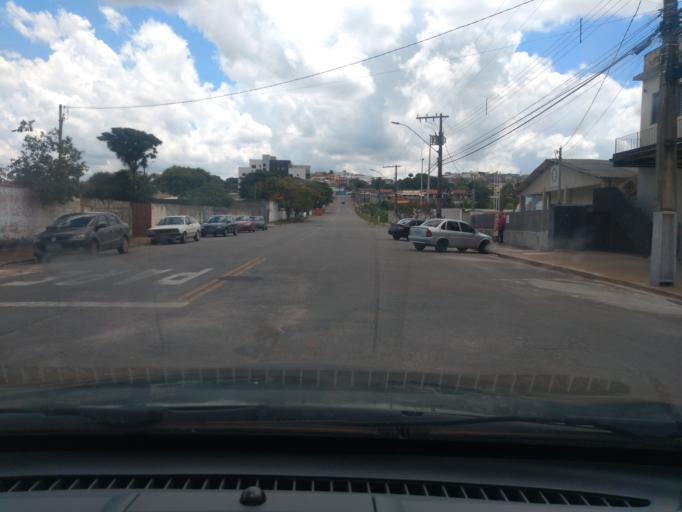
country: BR
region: Minas Gerais
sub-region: Tres Coracoes
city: Tres Coracoes
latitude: -21.6722
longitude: -45.2676
